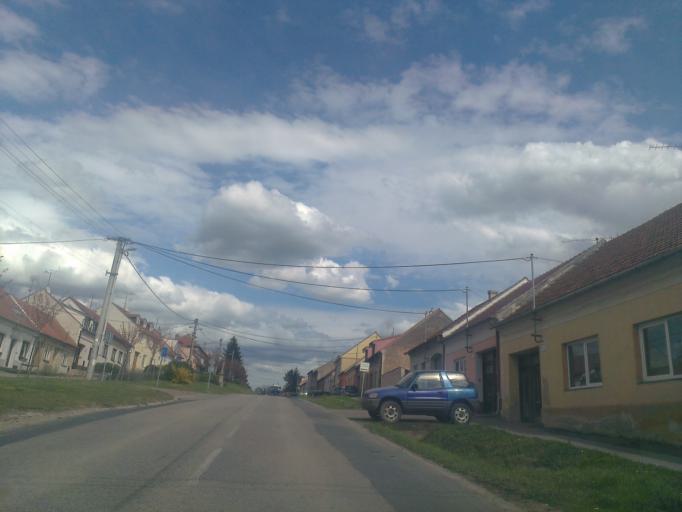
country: CZ
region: South Moravian
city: Zelesice
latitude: 49.1176
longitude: 16.5874
